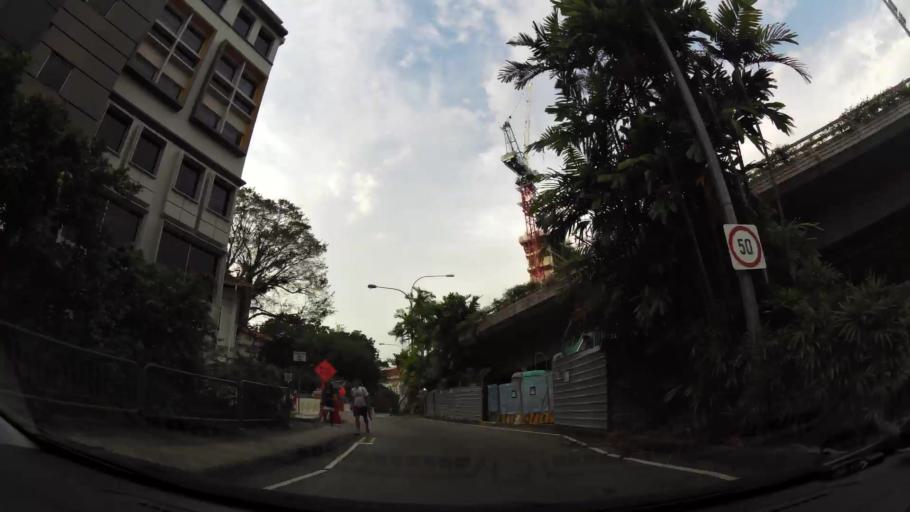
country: SG
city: Singapore
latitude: 1.2964
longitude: 103.8437
